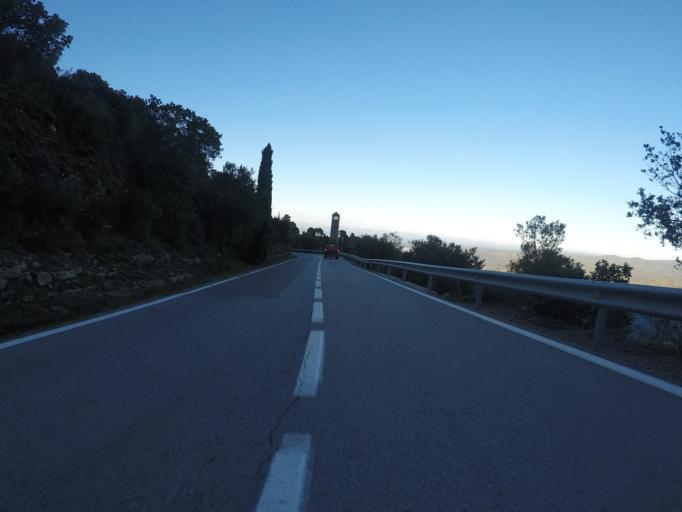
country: ES
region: Catalonia
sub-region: Provincia de Barcelona
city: Monistrol de Montserrat
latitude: 41.6068
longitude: 1.8262
